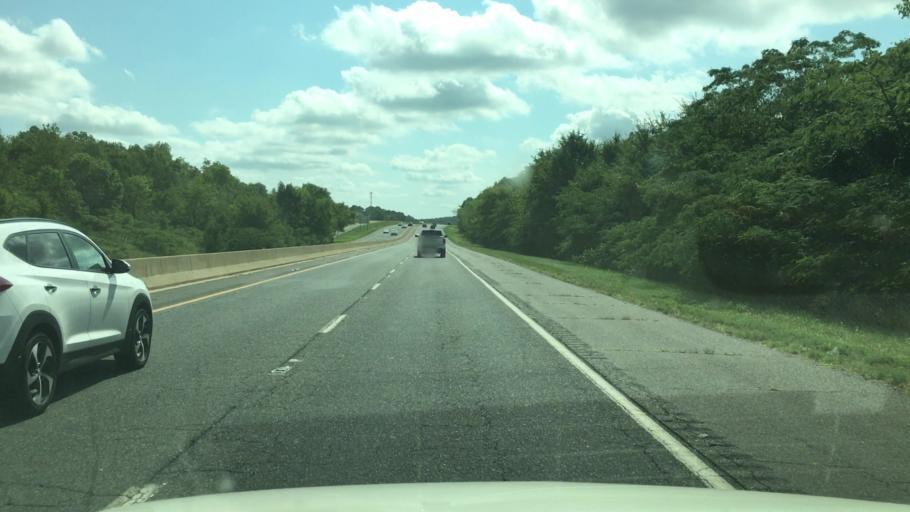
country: US
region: Arkansas
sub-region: Garland County
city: Rockwell
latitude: 34.4710
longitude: -93.1038
